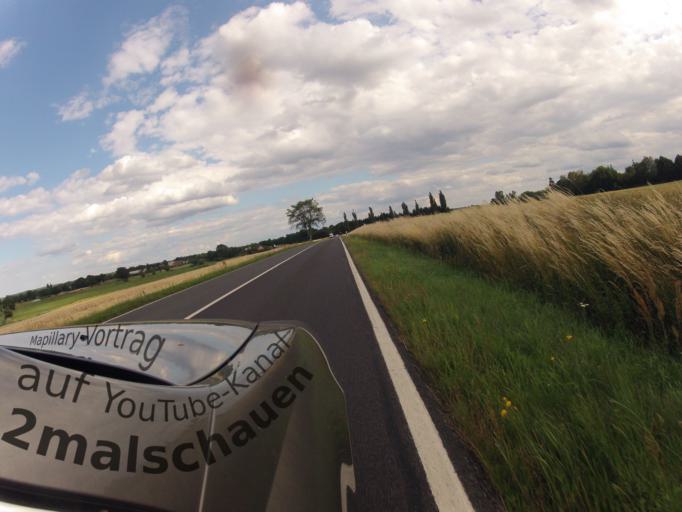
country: DE
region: Mecklenburg-Vorpommern
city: Seebad Bansin
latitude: 53.8899
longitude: 14.0793
